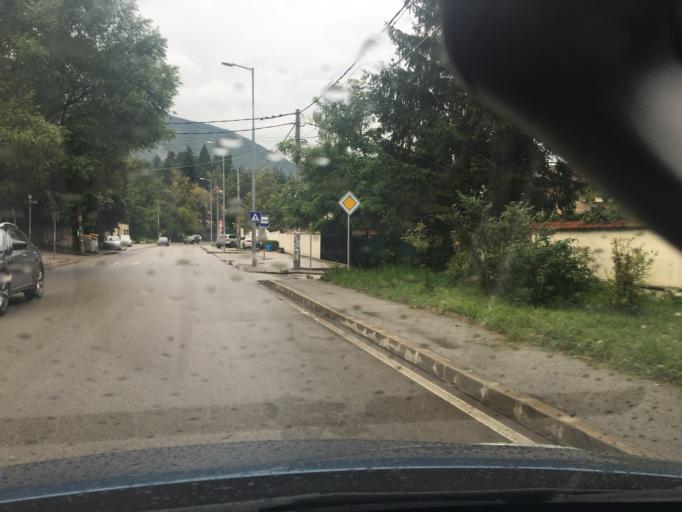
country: BG
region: Sofia-Capital
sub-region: Stolichna Obshtina
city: Sofia
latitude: 42.6354
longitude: 23.3002
